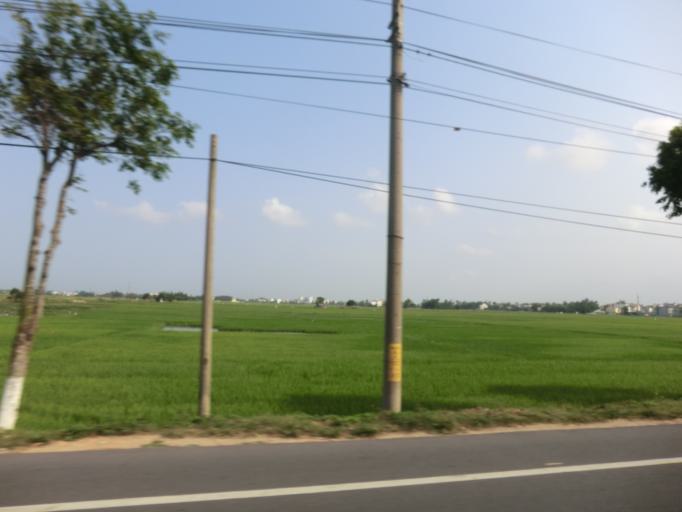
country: VN
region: Quang Nam
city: Hoi An
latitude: 15.8944
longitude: 108.3333
